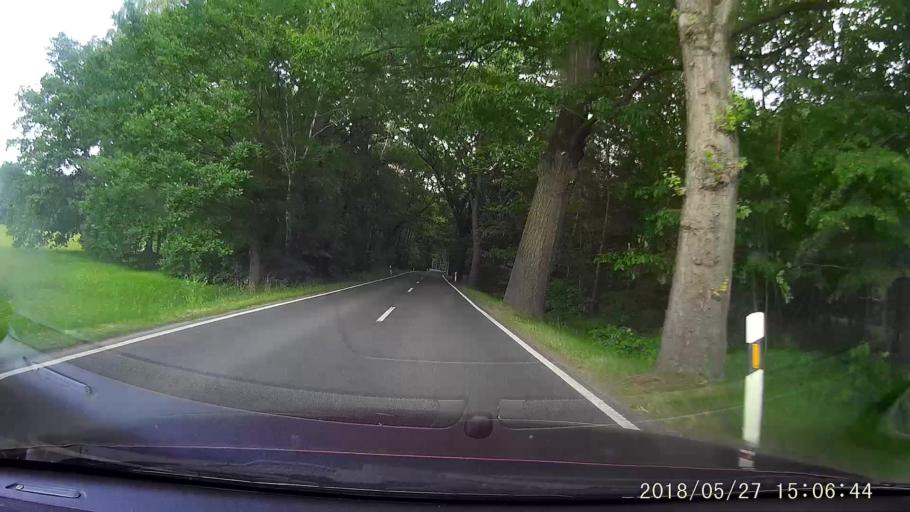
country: DE
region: Saxony
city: Quitzdorf
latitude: 51.3024
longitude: 14.7348
